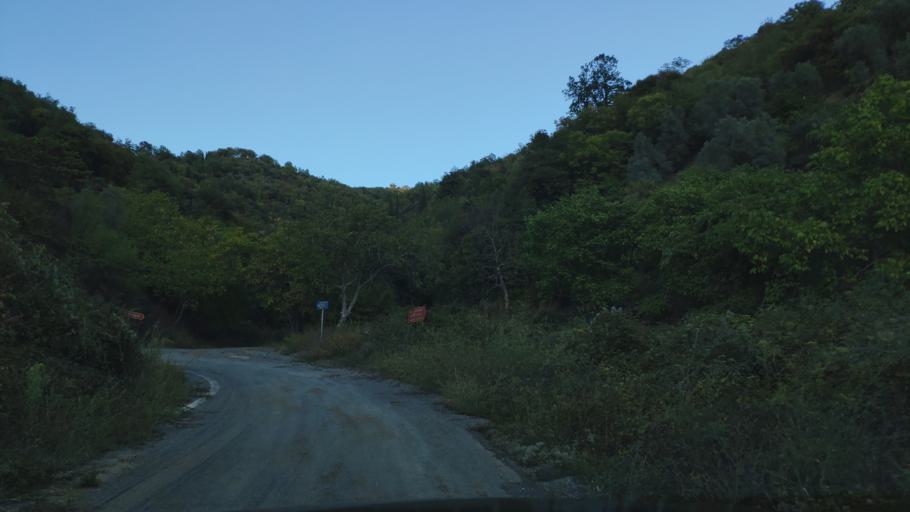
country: GR
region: Peloponnese
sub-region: Nomos Arkadias
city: Dimitsana
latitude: 37.5673
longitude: 22.0475
